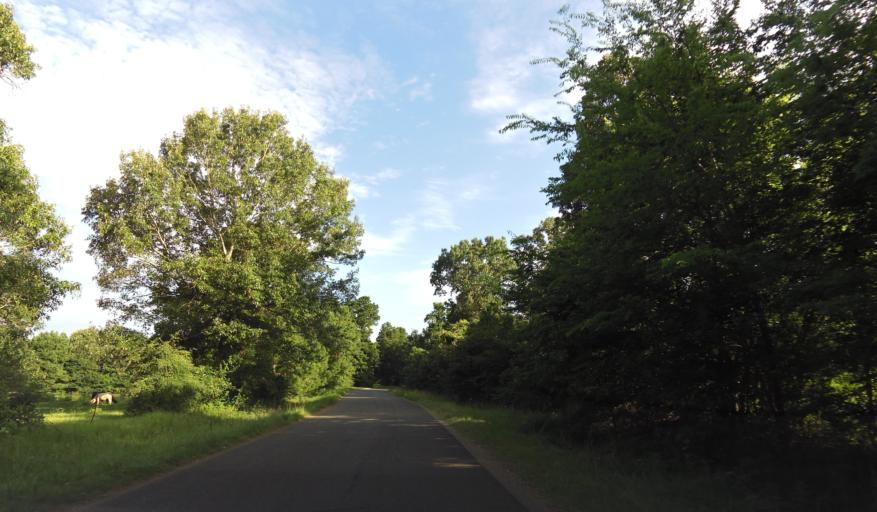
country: US
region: Louisiana
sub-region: Sabine Parish
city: Zwolle
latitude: 31.4868
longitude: -93.6923
